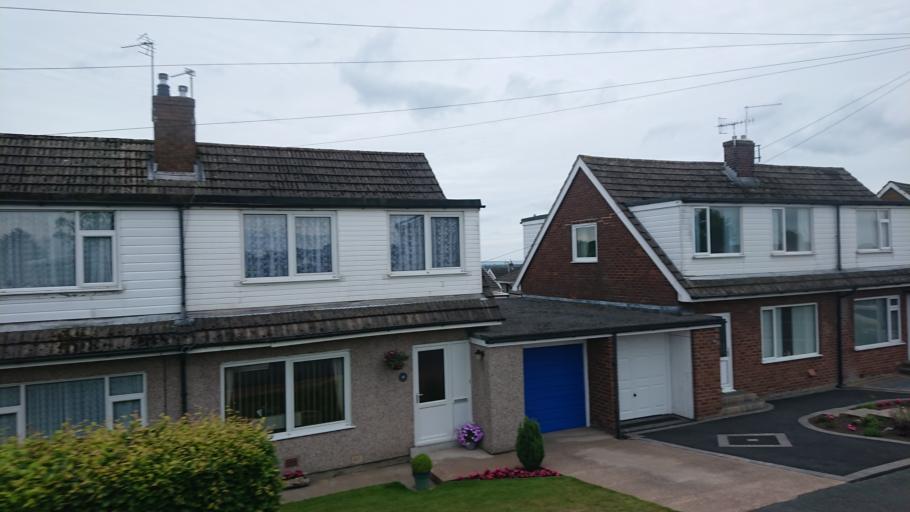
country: GB
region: England
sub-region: Lancashire
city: Lancaster
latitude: 54.0269
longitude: -2.7852
